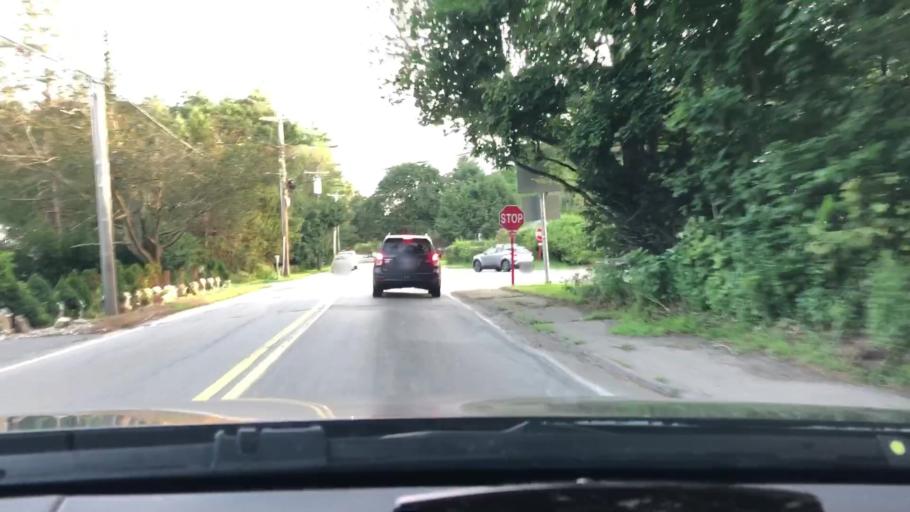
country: US
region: Massachusetts
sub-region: Norfolk County
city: Millis-Clicquot
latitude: 42.1569
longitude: -71.3517
